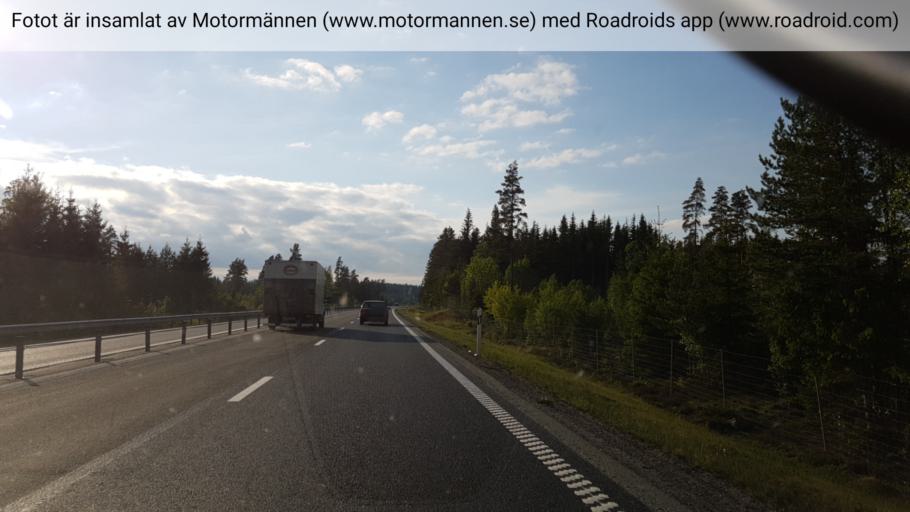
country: SE
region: Joenkoeping
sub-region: Nassjo Kommun
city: Malmback
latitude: 57.6896
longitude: 14.4558
